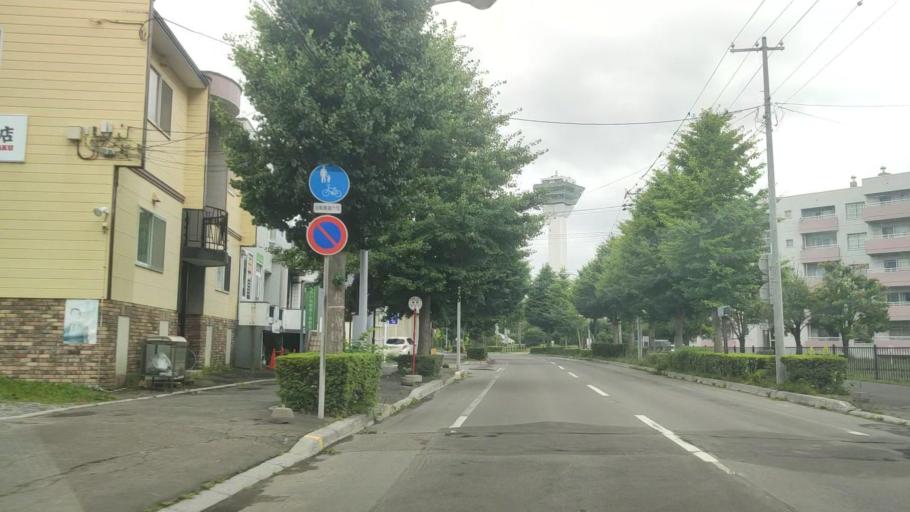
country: JP
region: Hokkaido
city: Hakodate
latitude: 41.7940
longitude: 140.7586
